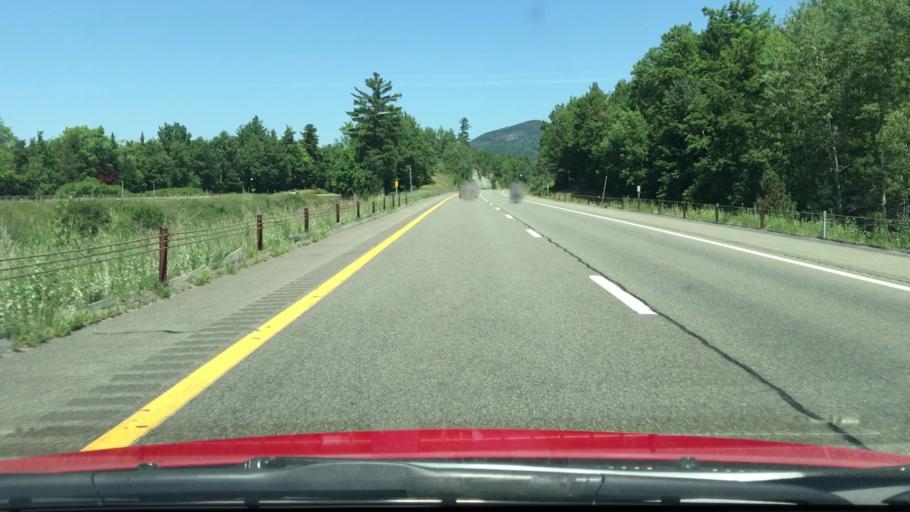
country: US
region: New York
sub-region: Essex County
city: Elizabethtown
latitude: 44.3465
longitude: -73.5330
